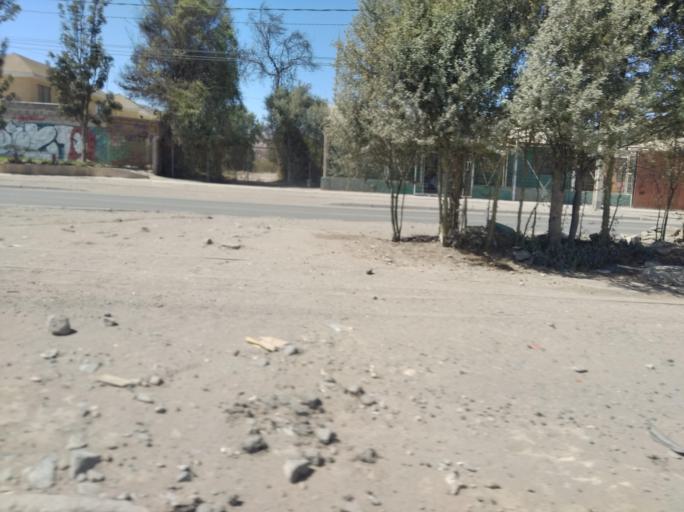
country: CL
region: Atacama
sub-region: Provincia de Copiapo
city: Copiapo
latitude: -27.4015
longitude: -70.2922
